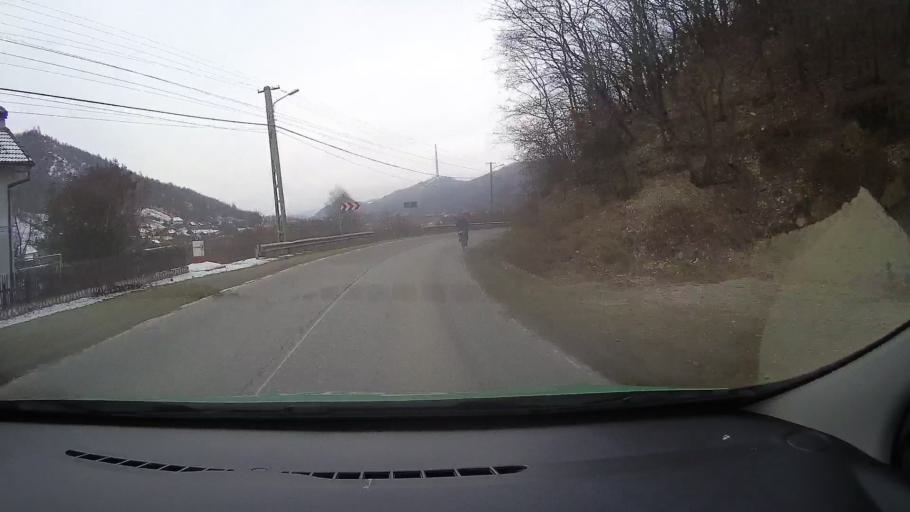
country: RO
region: Alba
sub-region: Oras Zlatna
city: Zlatna
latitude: 46.0930
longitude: 23.2560
